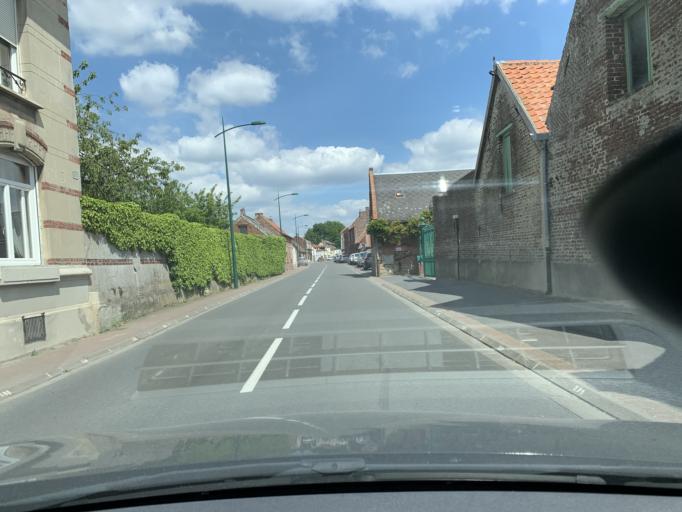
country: FR
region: Nord-Pas-de-Calais
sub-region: Departement du Nord
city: Arleux
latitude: 50.2762
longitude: 3.1010
